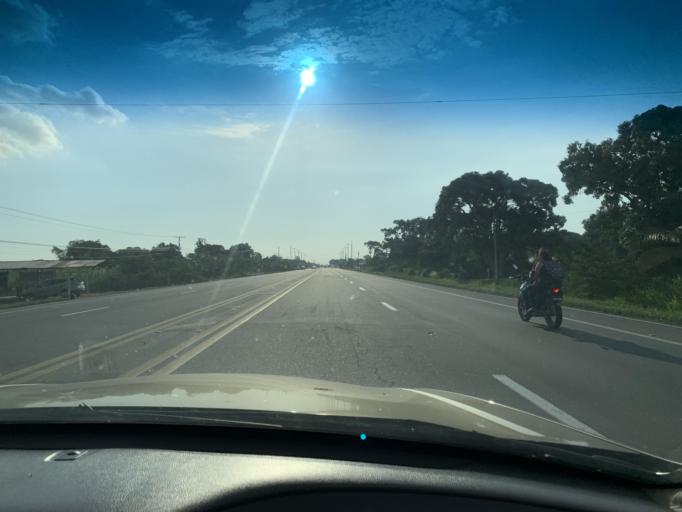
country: EC
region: Guayas
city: Naranjito
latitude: -2.2569
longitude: -79.5843
